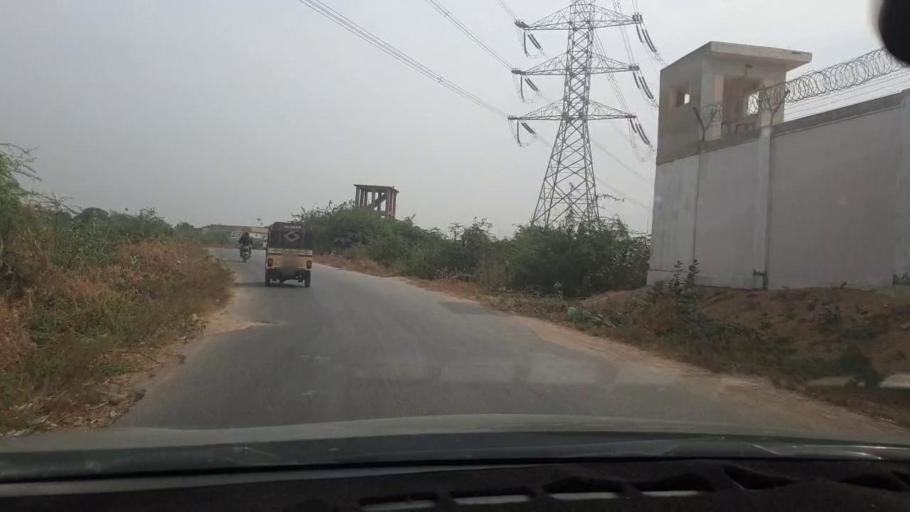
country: PK
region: Sindh
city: Malir Cantonment
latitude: 24.9103
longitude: 67.2844
